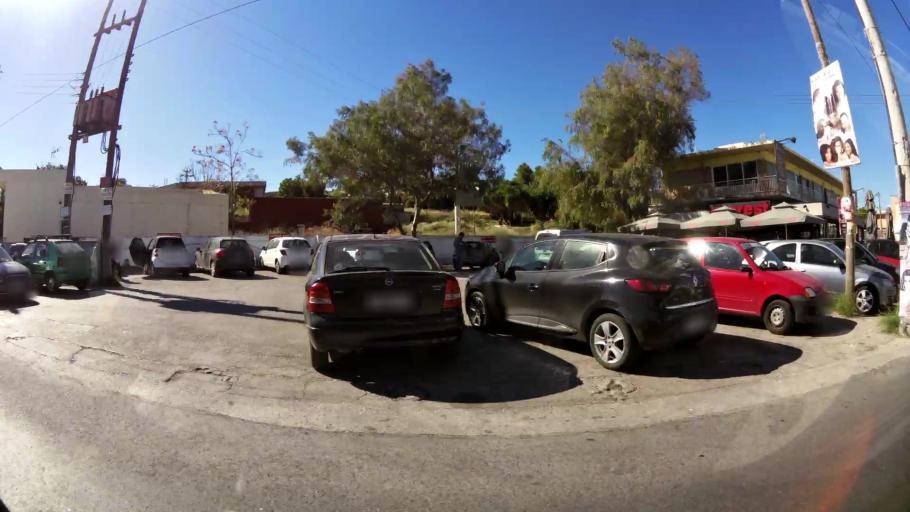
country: GR
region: Attica
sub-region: Nomarchia Anatolikis Attikis
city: Koropi
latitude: 37.8934
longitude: 23.8811
